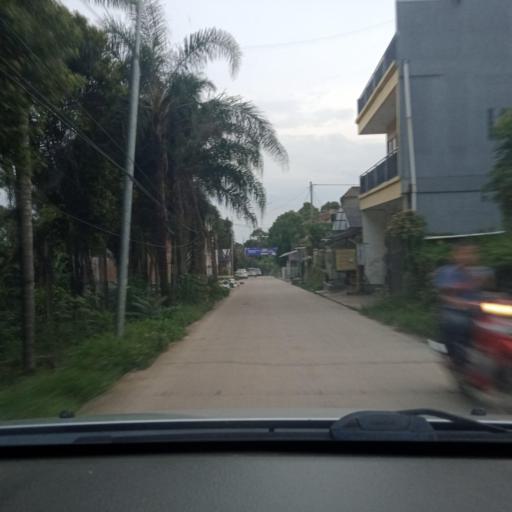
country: ID
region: West Java
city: Lembang
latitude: -6.8306
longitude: 107.5858
